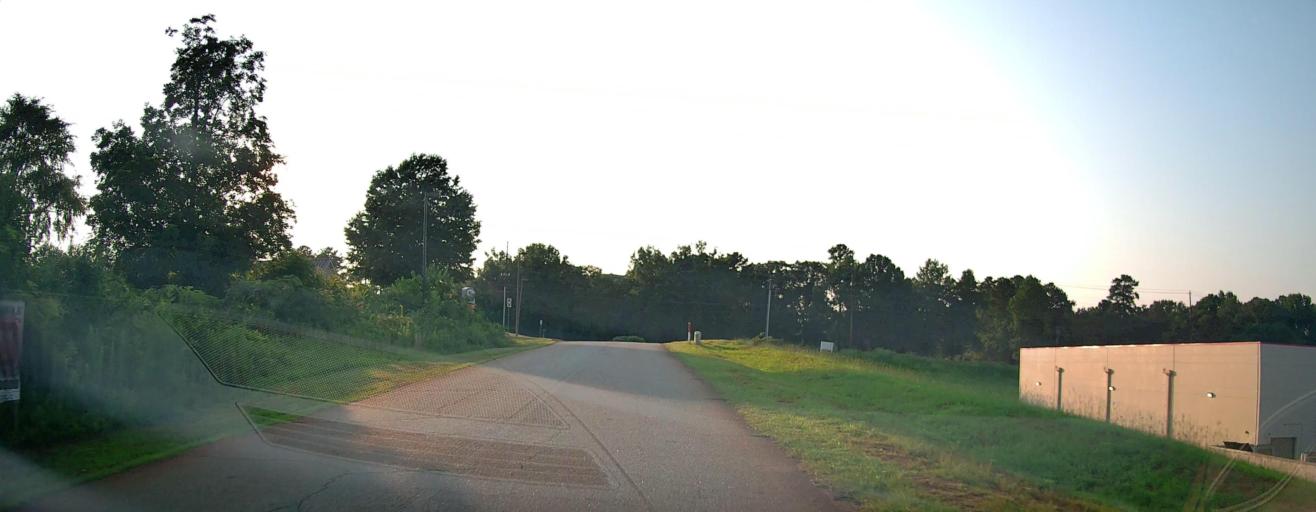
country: US
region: Georgia
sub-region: Bibb County
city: Macon
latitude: 32.9288
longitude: -83.7284
